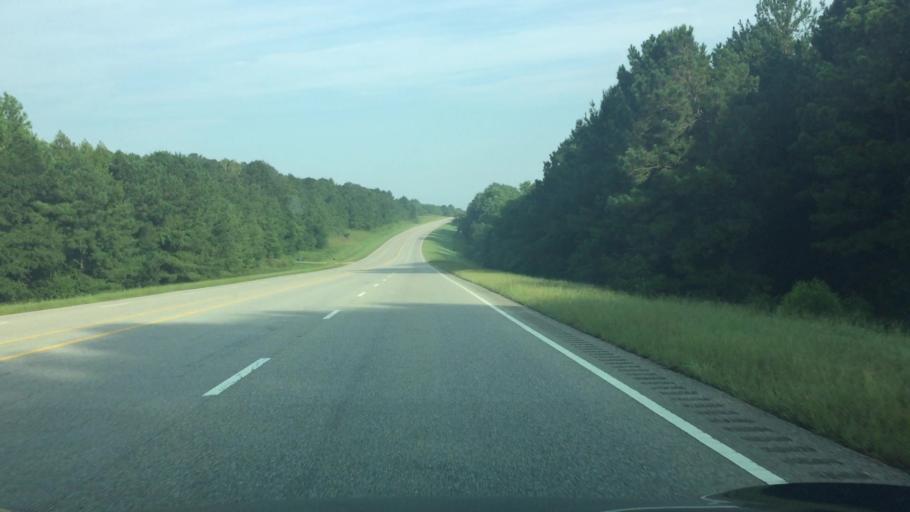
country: US
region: Alabama
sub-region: Covington County
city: Andalusia
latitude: 31.4483
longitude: -86.6223
